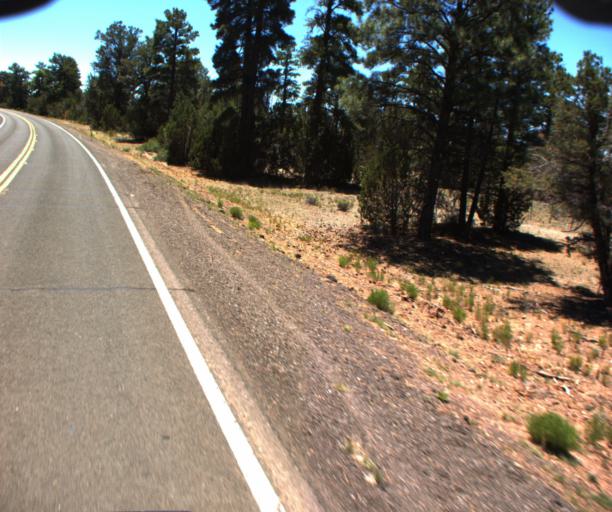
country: US
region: Arizona
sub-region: Gila County
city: Star Valley
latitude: 34.6752
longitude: -111.1114
